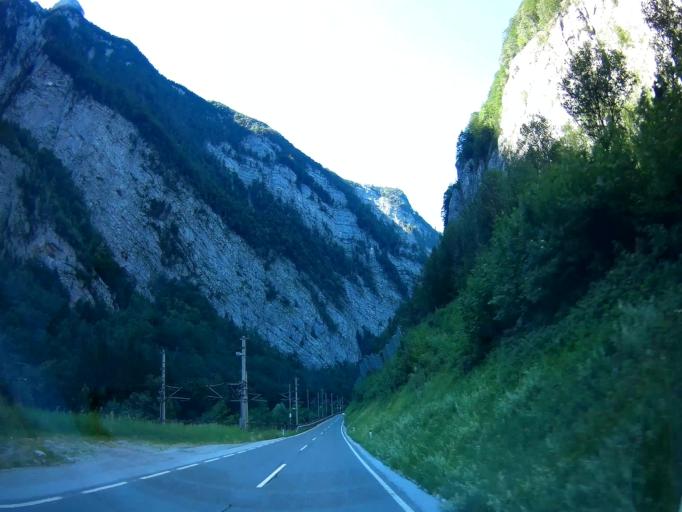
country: AT
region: Salzburg
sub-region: Politischer Bezirk Hallein
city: Golling an der Salzach
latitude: 47.5560
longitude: 13.1672
